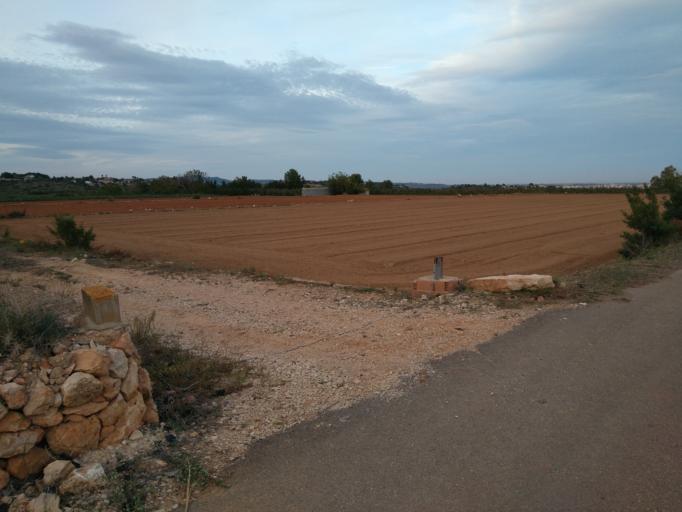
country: ES
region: Valencia
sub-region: Provincia de Valencia
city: Benimodo
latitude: 39.2001
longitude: -0.5809
